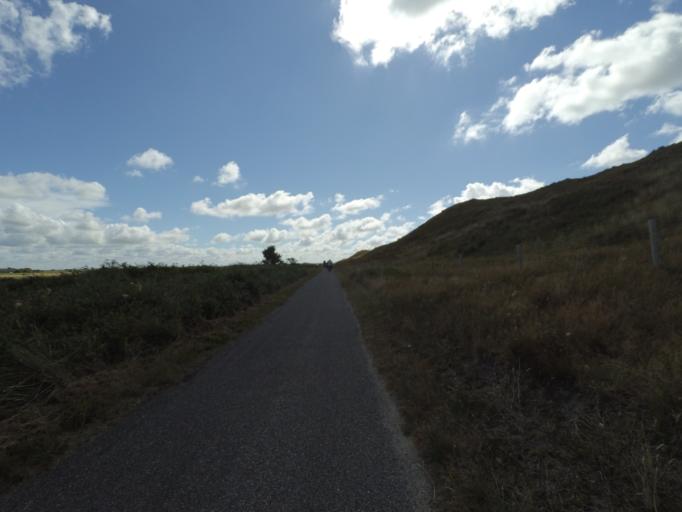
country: NL
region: North Holland
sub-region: Gemeente Texel
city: Den Burg
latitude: 53.1233
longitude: 4.8075
